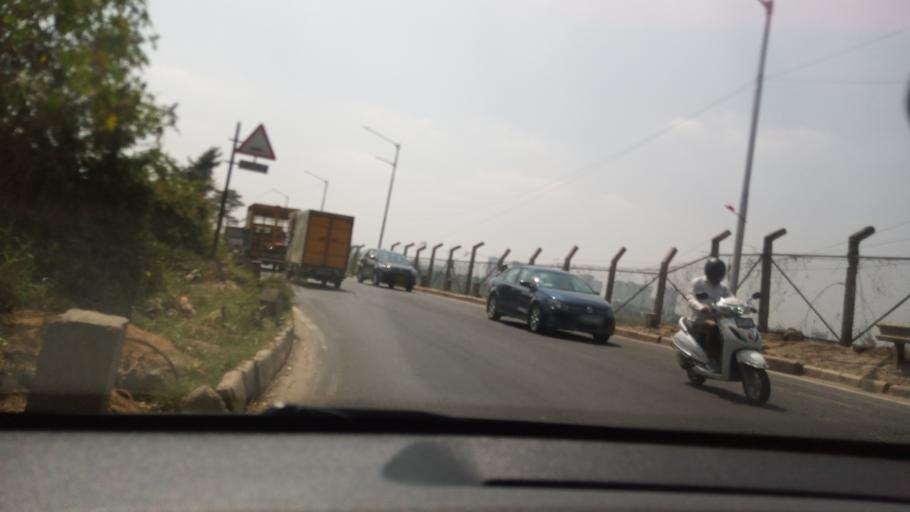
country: IN
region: Karnataka
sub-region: Bangalore Rural
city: Hoskote
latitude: 12.9534
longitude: 77.7441
